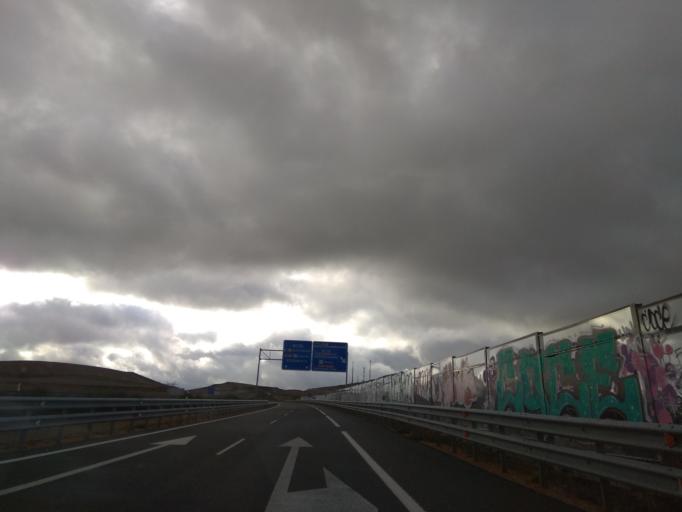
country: ES
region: Castille and Leon
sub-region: Provincia de Burgos
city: Sotragero
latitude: 42.3987
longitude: -3.6987
